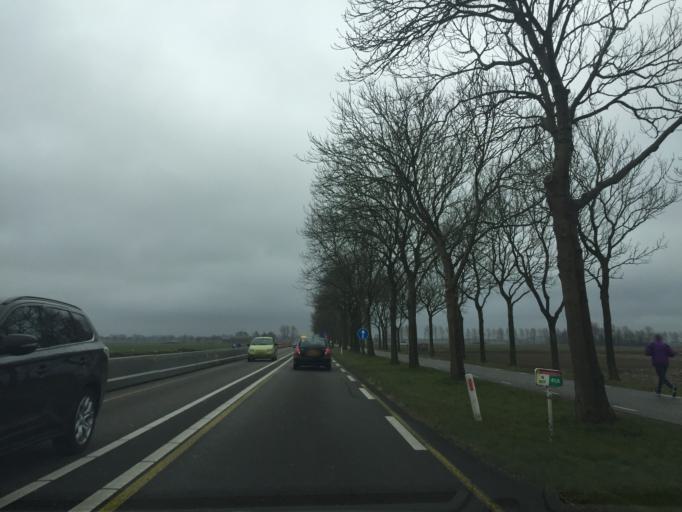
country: NL
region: South Holland
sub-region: Gemeente Kaag en Braassem
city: Oude Wetering
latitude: 52.1750
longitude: 4.6699
